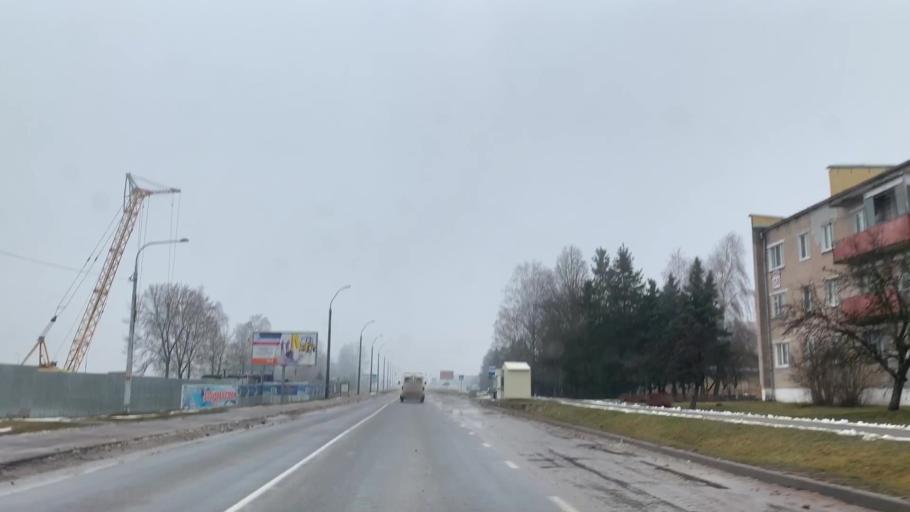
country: BY
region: Minsk
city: Nyasvizh
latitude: 53.2350
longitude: 26.6456
